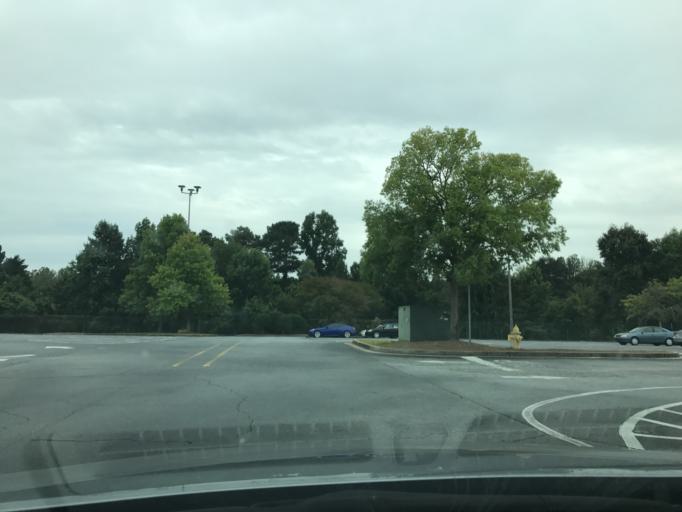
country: US
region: Georgia
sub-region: DeKalb County
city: Scottdale
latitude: 33.8069
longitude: -84.2774
